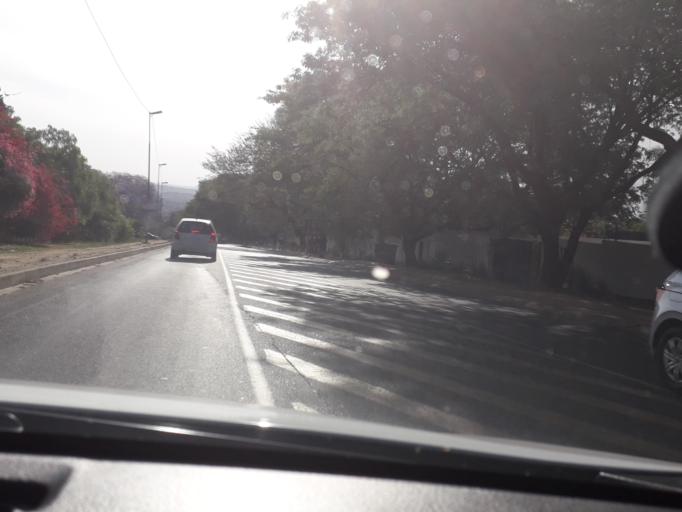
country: ZA
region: Gauteng
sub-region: City of Johannesburg Metropolitan Municipality
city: Diepsloot
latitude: -26.0329
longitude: 28.0085
